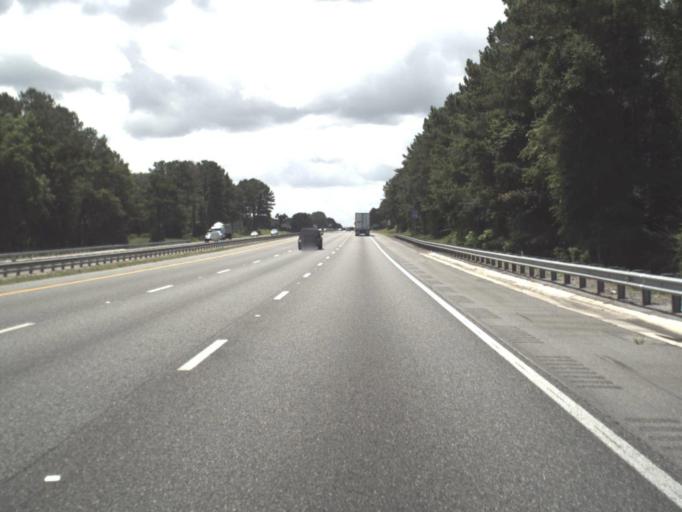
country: US
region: Florida
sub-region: Columbia County
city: Lake City
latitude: 30.1118
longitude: -82.6526
